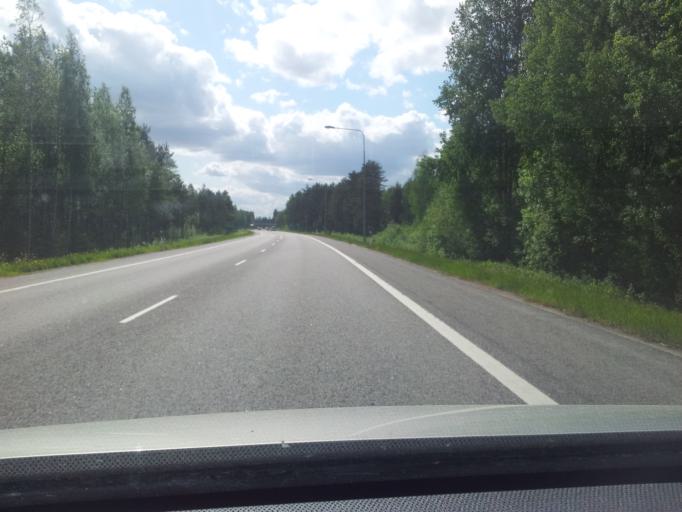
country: FI
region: Kymenlaakso
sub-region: Kouvola
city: Kouvola
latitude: 60.8785
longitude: 26.6721
